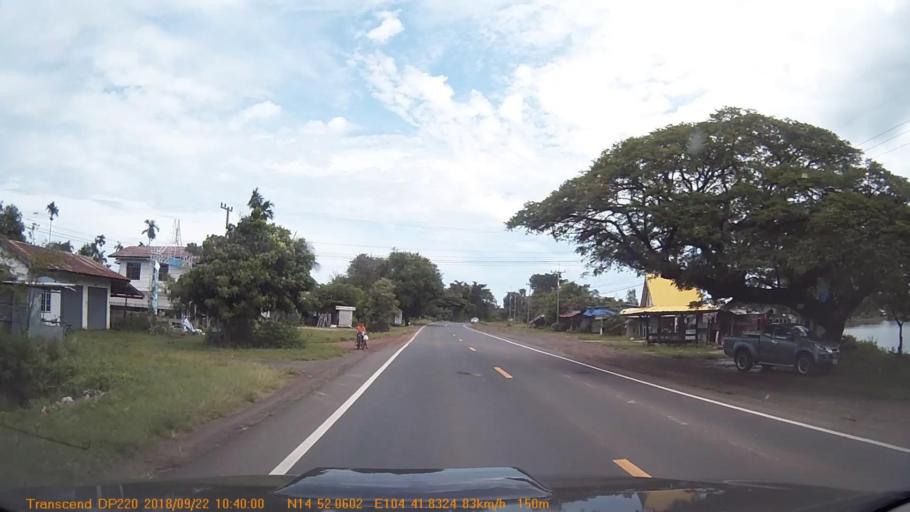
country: TH
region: Sisaket
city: Non Kho
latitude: 14.8679
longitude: 104.6972
